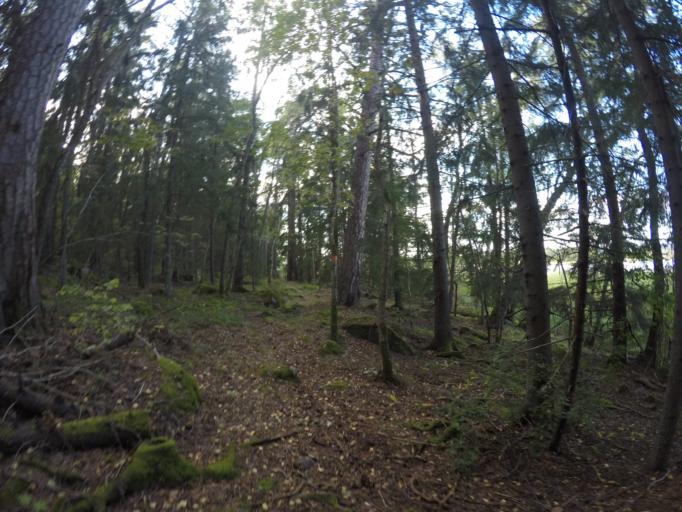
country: SE
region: Vaestmanland
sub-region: Hallstahammars Kommun
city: Kolback
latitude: 59.4819
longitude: 16.2318
